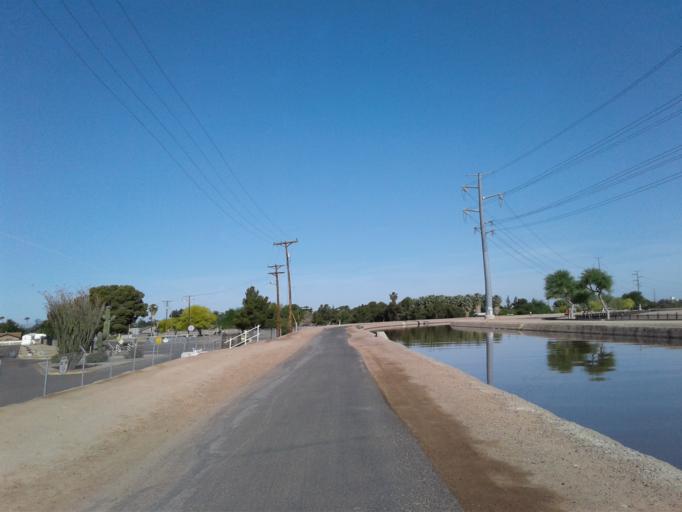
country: US
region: Arizona
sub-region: Maricopa County
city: Glendale
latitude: 33.5889
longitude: -112.1621
